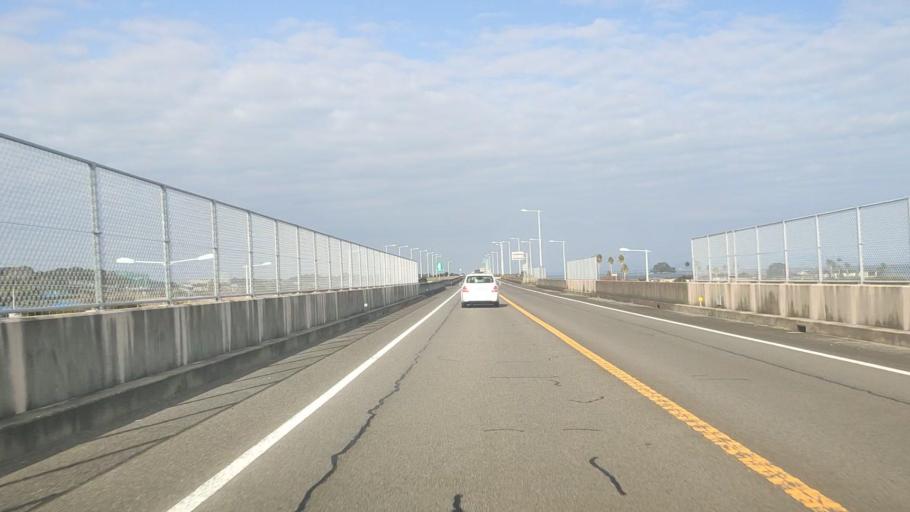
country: JP
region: Nagasaki
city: Shimabara
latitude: 32.7445
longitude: 130.3725
